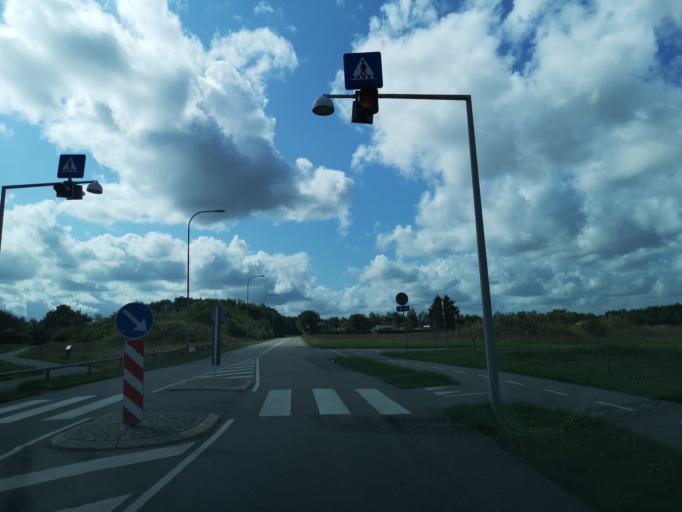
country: DK
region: Central Jutland
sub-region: Holstebro Kommune
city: Holstebro
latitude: 56.3833
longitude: 8.5760
